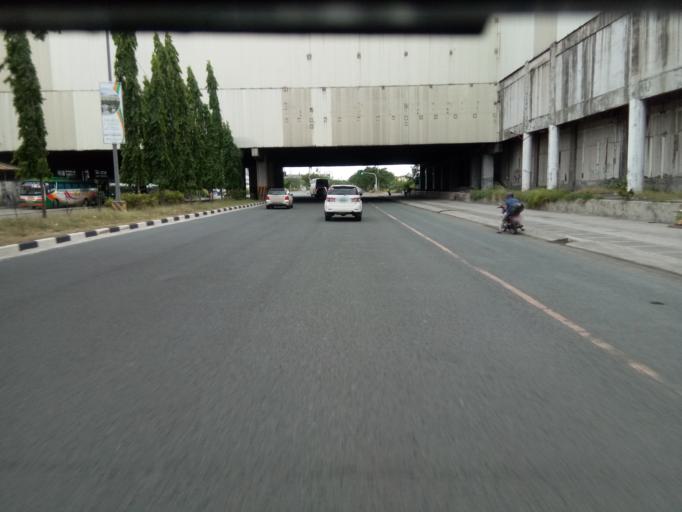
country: PH
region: Metro Manila
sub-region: Makati City
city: Makati City
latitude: 14.5162
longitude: 120.9905
